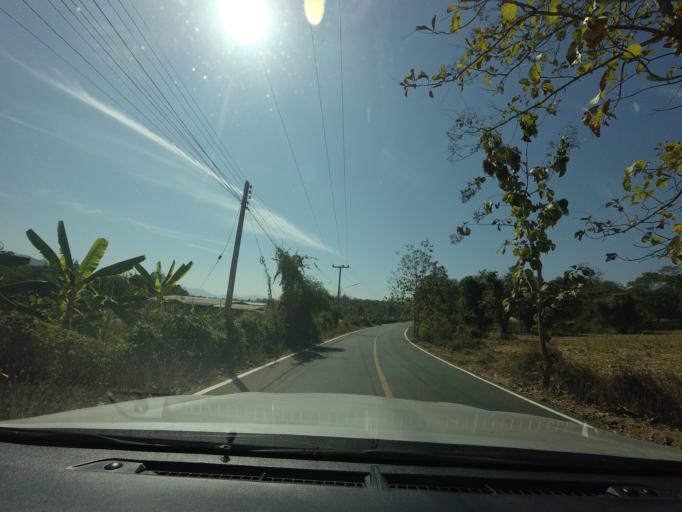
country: TH
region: Mae Hong Son
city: Wiang Nuea
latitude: 19.3822
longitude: 98.4376
